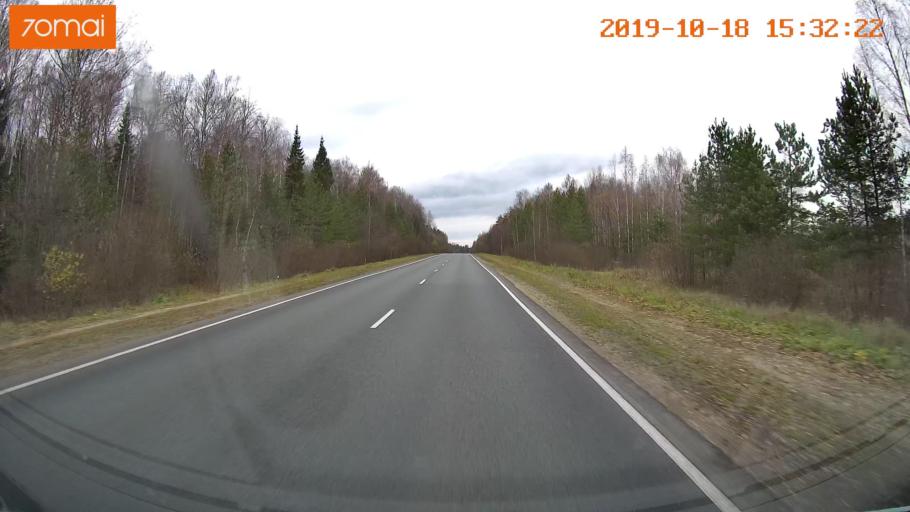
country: RU
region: Vladimir
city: Anopino
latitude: 55.8253
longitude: 40.6546
